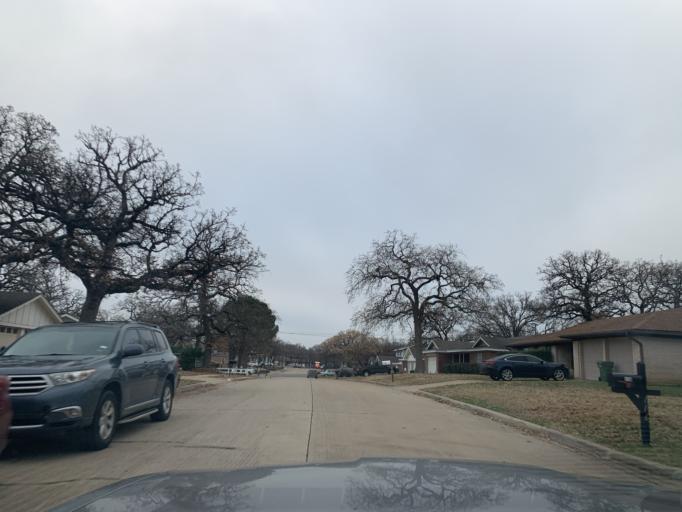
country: US
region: Texas
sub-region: Tarrant County
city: Bedford
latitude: 32.8376
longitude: -97.1564
